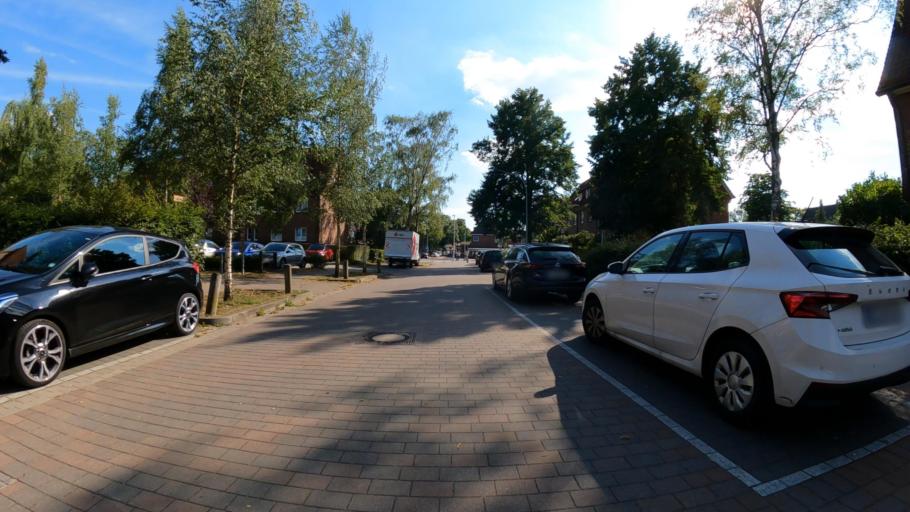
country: DE
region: Schleswig-Holstein
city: Norderstedt
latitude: 53.6830
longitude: 9.9815
